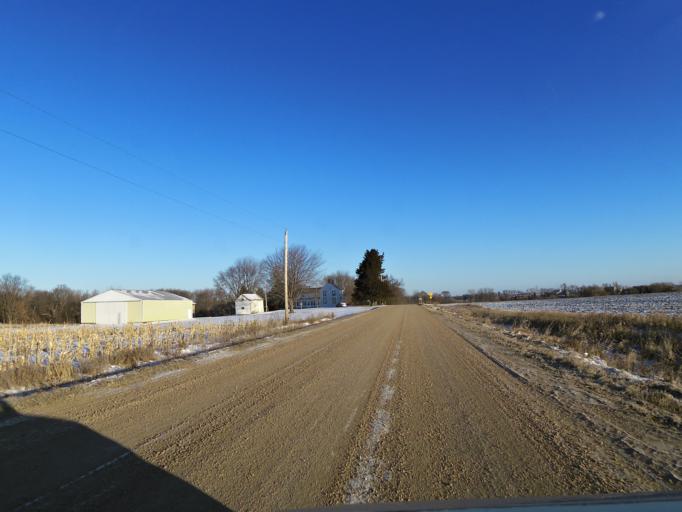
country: US
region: Minnesota
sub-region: Scott County
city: Jordan
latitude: 44.6700
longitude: -93.5418
